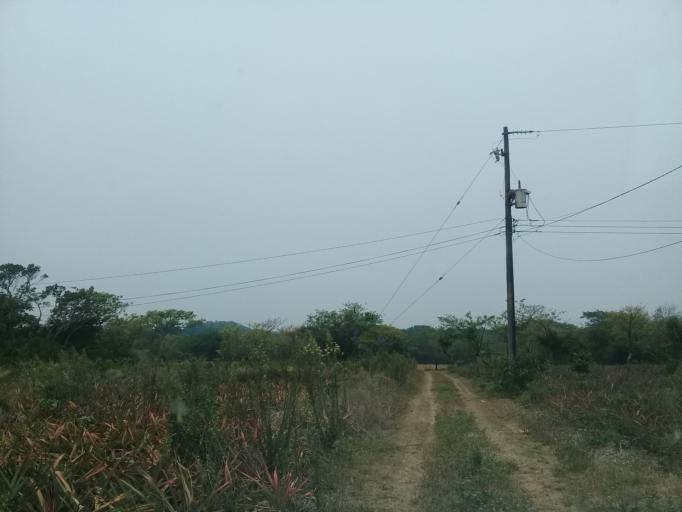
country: MX
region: Veracruz
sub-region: Medellin
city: La Laguna y Monte del Castillo
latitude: 18.9737
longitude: -96.1384
